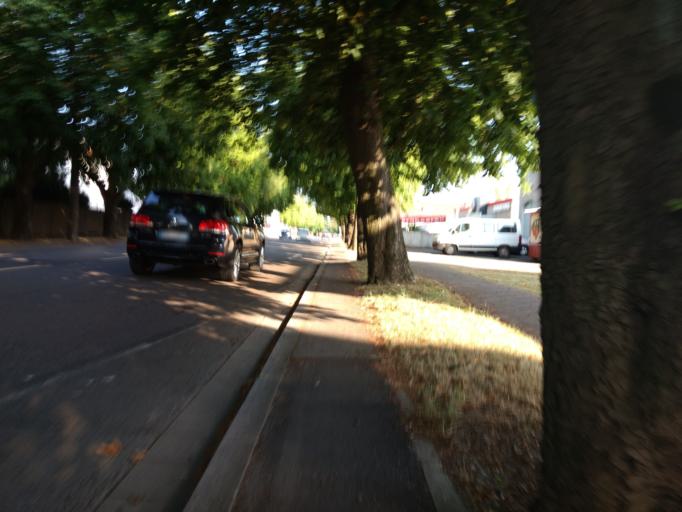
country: DE
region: Saarland
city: Saarlouis
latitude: 49.3187
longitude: 6.7342
